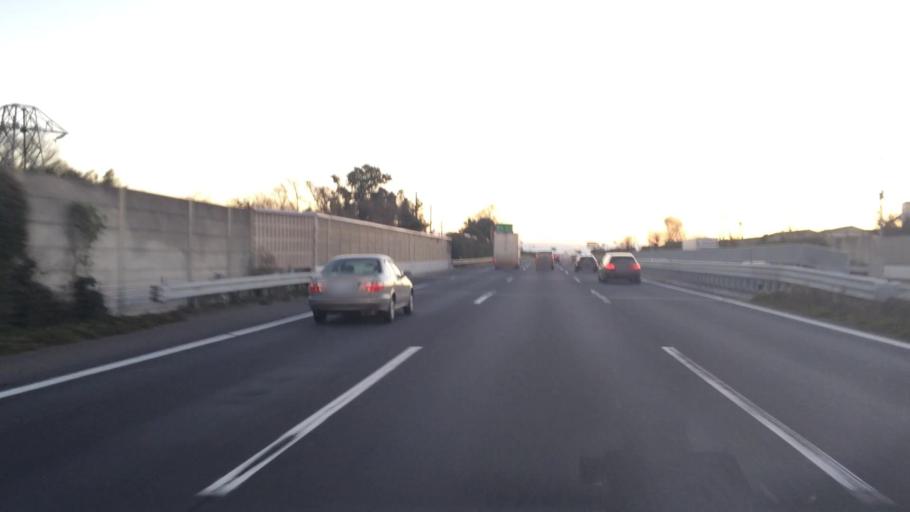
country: JP
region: Gunma
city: Tatebayashi
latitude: 36.2367
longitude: 139.5754
